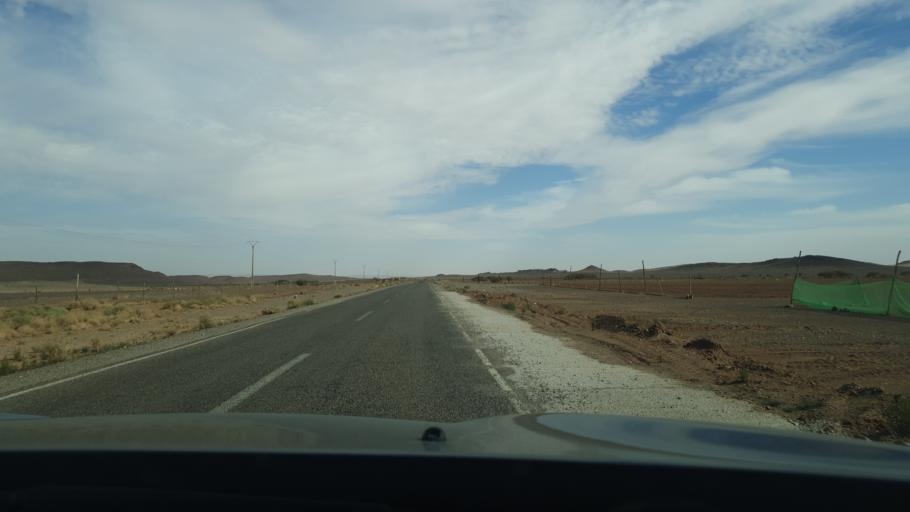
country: MA
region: Meknes-Tafilalet
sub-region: Errachidia
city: Goulmima
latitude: 31.5729
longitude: -4.8030
